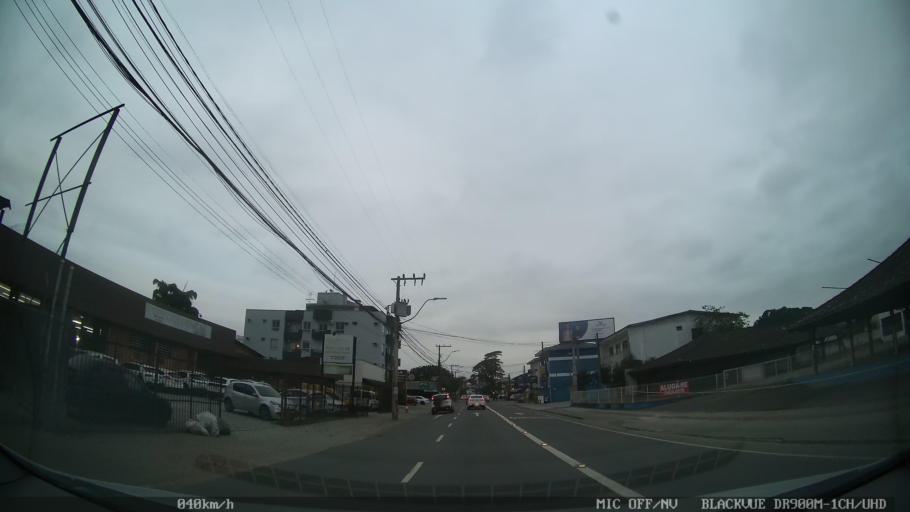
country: BR
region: Santa Catarina
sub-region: Joinville
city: Joinville
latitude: -26.2853
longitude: -48.8499
